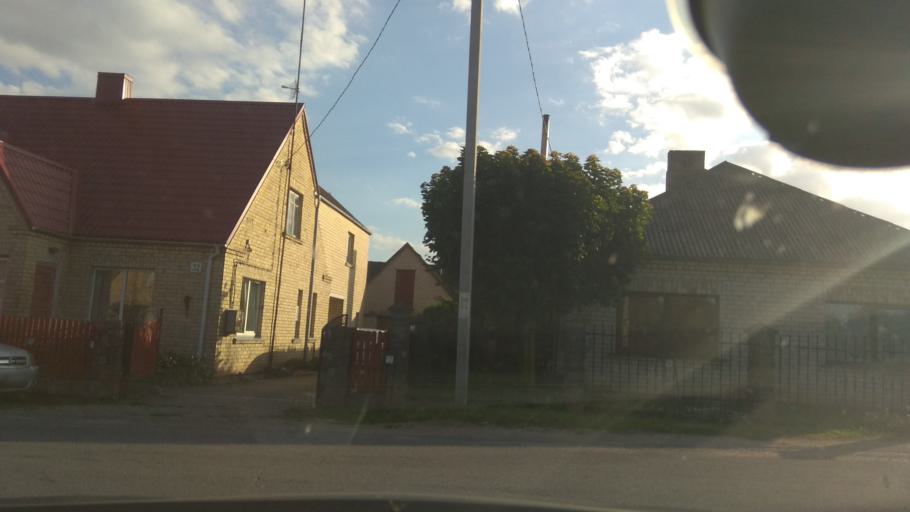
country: LT
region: Siauliu apskritis
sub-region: Joniskis
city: Joniskis
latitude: 56.2445
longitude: 23.6245
